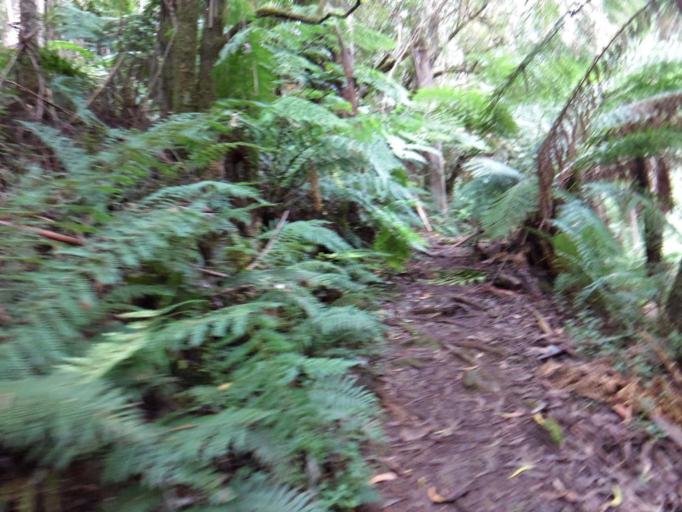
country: AU
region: Victoria
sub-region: Yarra Ranges
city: Kallista
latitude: -37.8803
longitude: 145.3806
